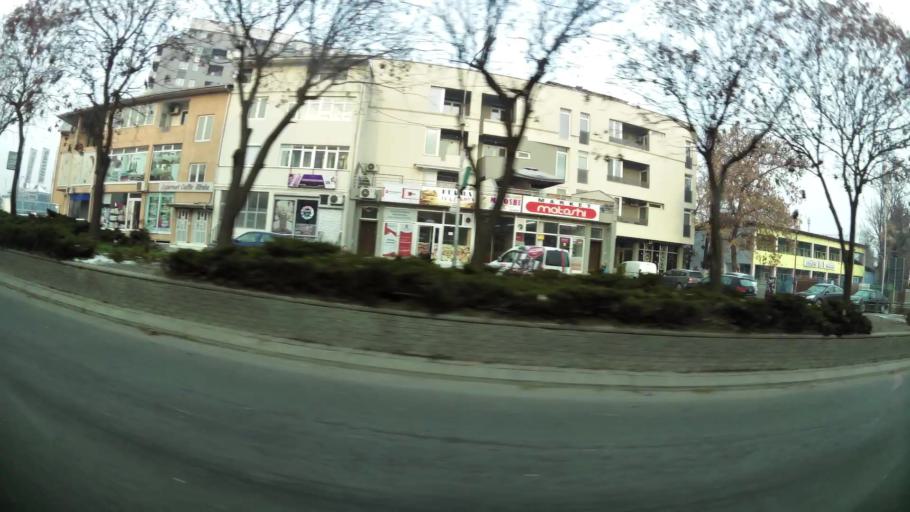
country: MK
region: Cair
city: Cair
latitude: 42.0060
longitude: 21.4418
